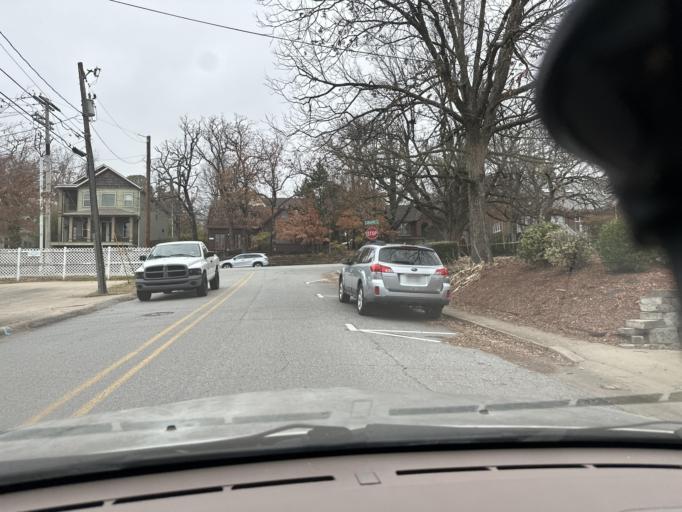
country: US
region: Arkansas
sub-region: Washington County
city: Fayetteville
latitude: 36.0682
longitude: -94.1607
